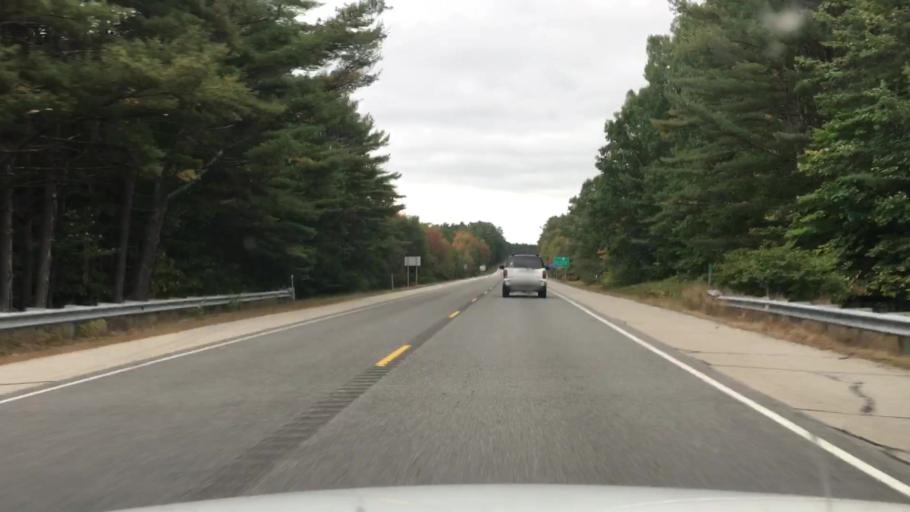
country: US
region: New Hampshire
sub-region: Carroll County
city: Ossipee
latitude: 43.7625
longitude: -71.1512
